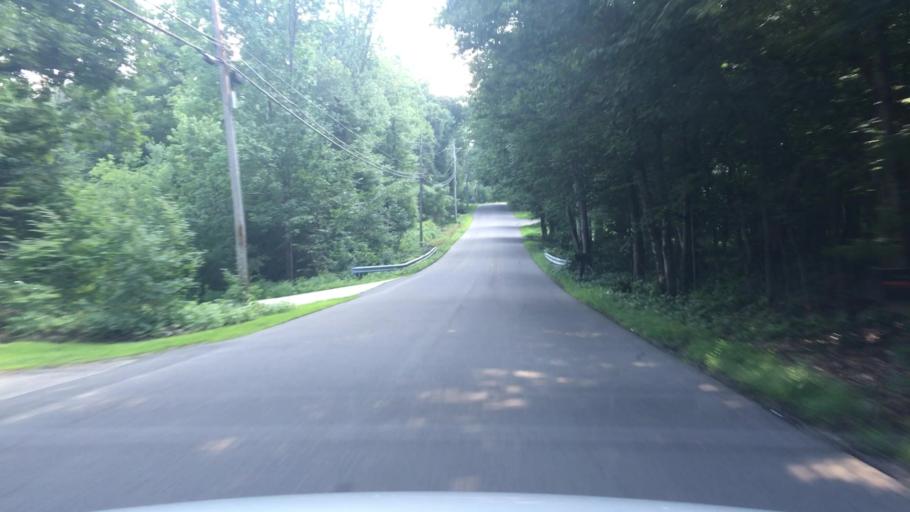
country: US
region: New Hampshire
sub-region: Rockingham County
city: Derry Village
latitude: 42.9264
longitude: -71.3160
